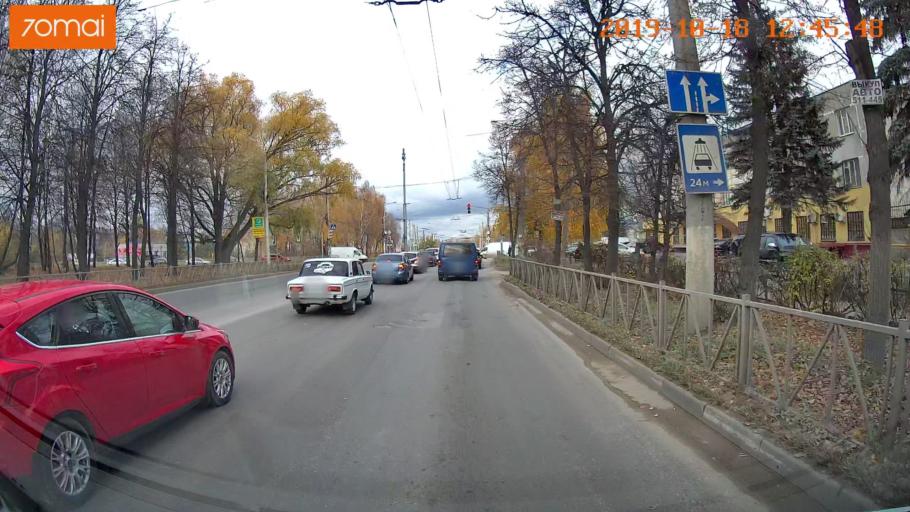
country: RU
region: Rjazan
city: Ryazan'
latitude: 54.6543
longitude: 39.6652
